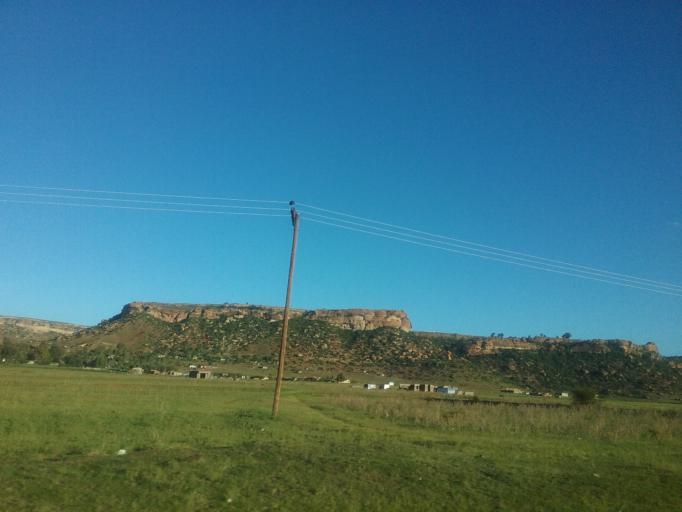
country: LS
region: Maseru
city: Maseru
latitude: -29.2626
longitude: 27.6022
